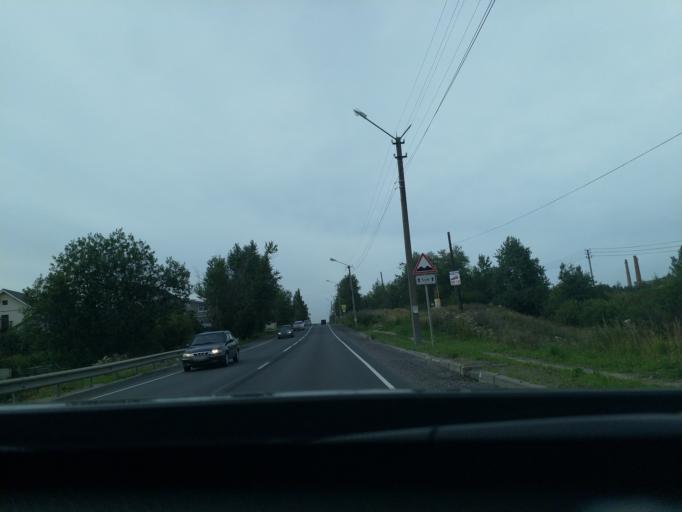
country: RU
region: Leningrad
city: Nikol'skoye
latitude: 59.7144
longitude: 30.7794
